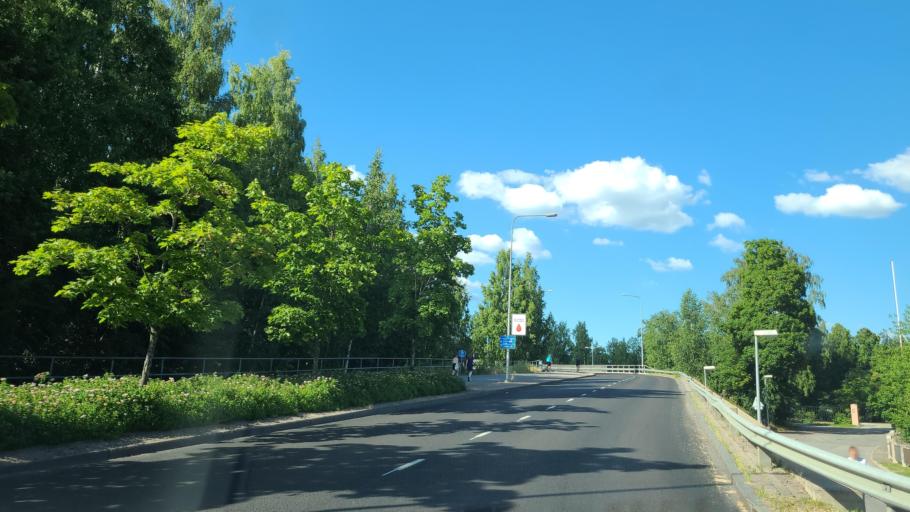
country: FI
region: Central Finland
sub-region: Jyvaeskylae
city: Jyvaeskylae
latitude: 62.2431
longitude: 25.7614
